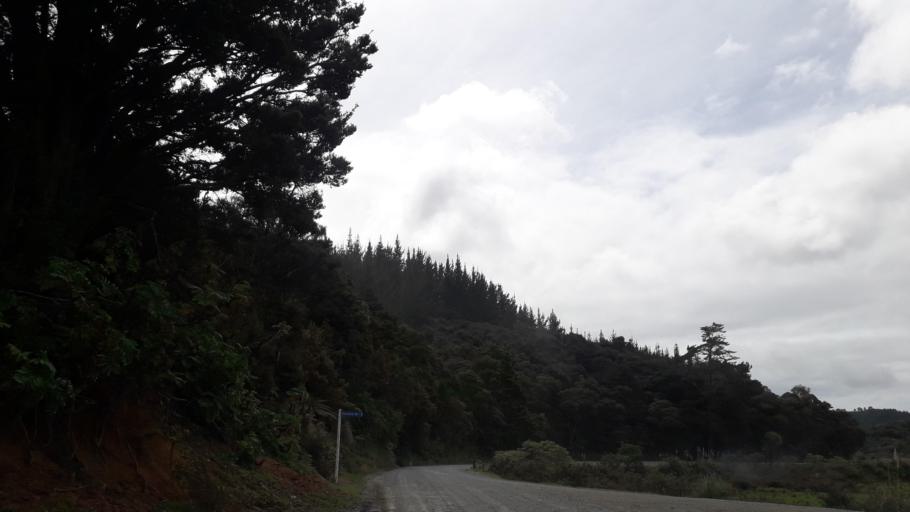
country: NZ
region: Northland
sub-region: Far North District
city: Taipa
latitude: -35.0415
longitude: 173.5644
